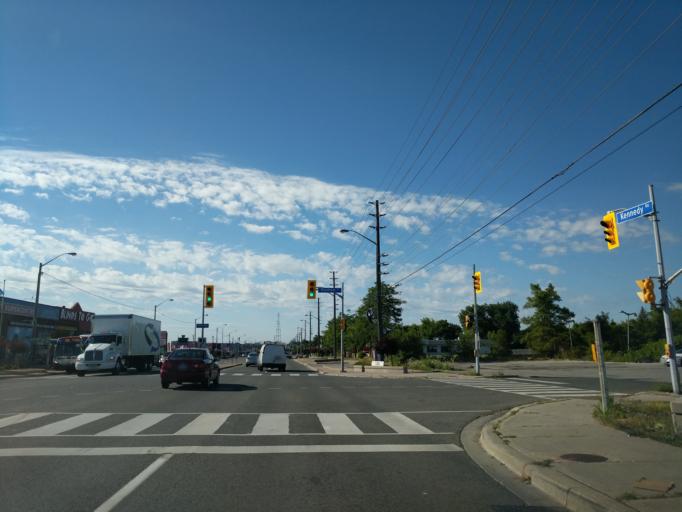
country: CA
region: Ontario
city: Scarborough
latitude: 43.7595
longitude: -79.2788
